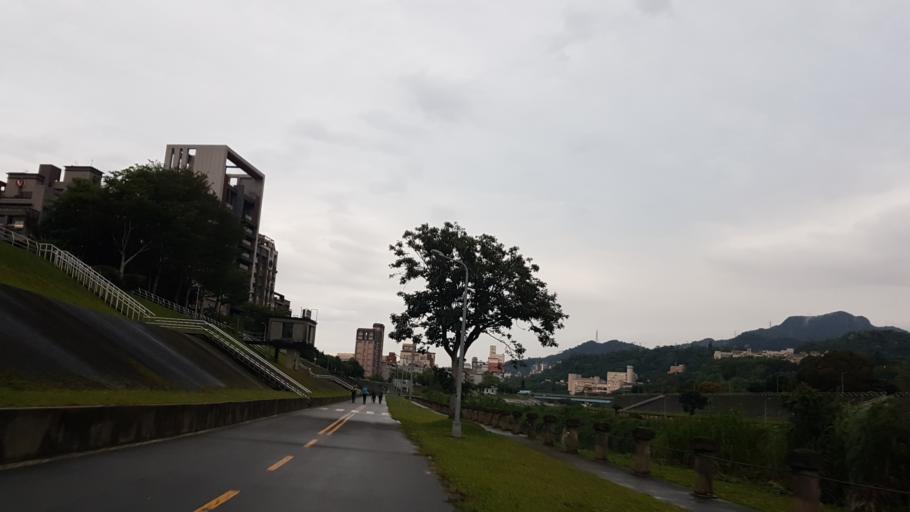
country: TW
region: Taipei
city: Taipei
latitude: 24.9800
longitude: 121.5620
